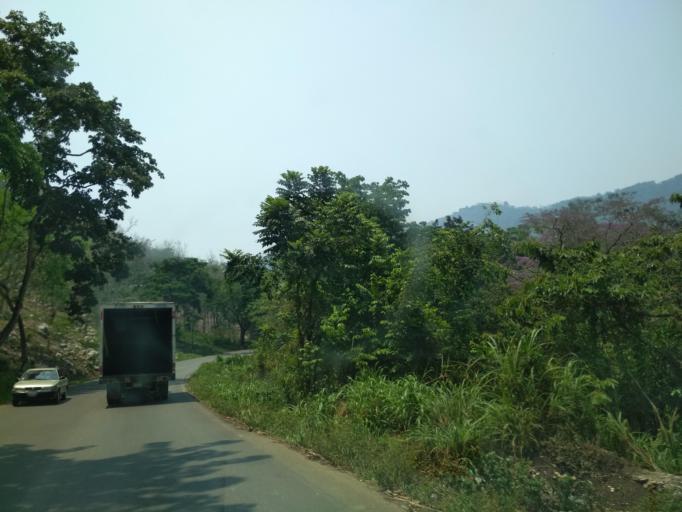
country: MX
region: Veracruz
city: Cosolapa
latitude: 18.6043
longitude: -96.6909
